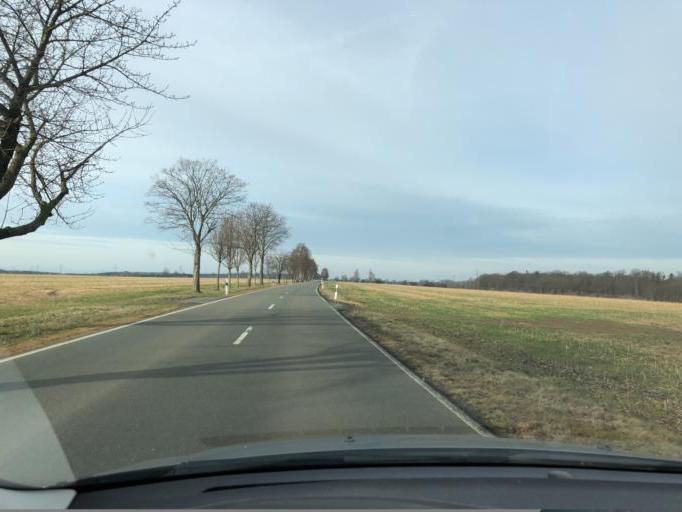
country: DE
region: Saxony-Anhalt
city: Bad Bibra
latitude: 51.1843
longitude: 11.5296
